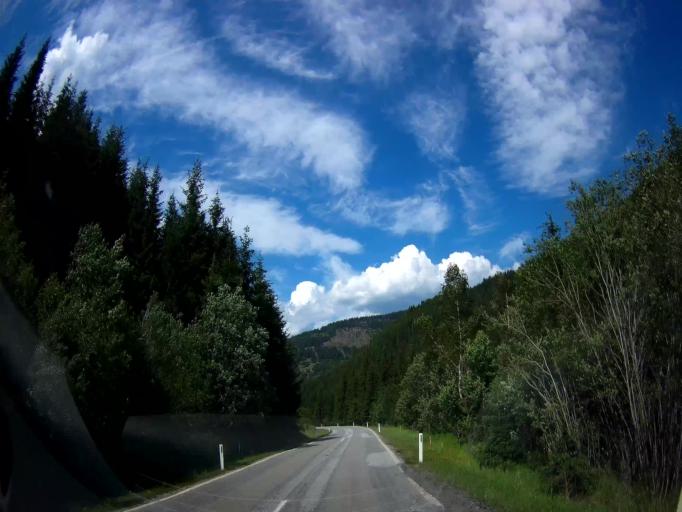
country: AT
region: Styria
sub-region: Politischer Bezirk Murau
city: Stadl an der Mur
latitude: 46.9930
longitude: 14.0148
